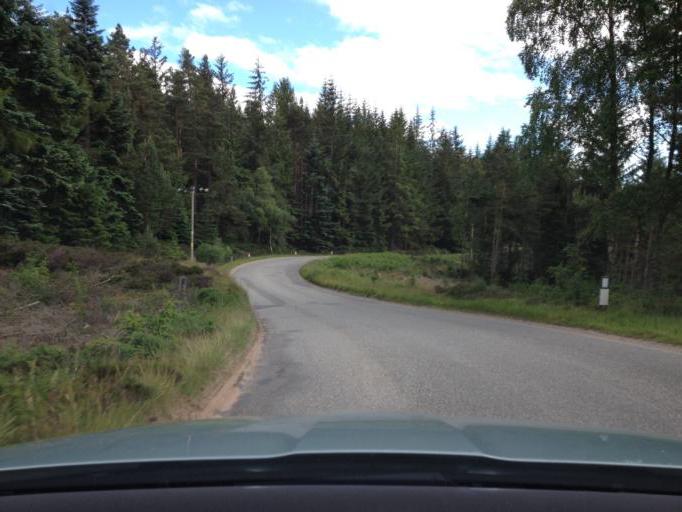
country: GB
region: Scotland
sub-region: Aberdeenshire
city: Banchory
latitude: 56.9878
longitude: -2.5758
